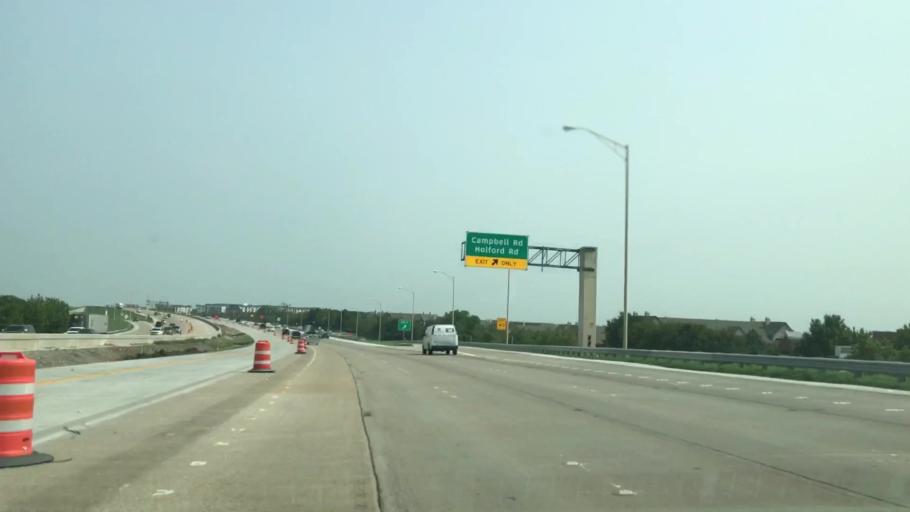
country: US
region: Texas
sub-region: Collin County
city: Plano
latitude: 32.9800
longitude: -96.6635
